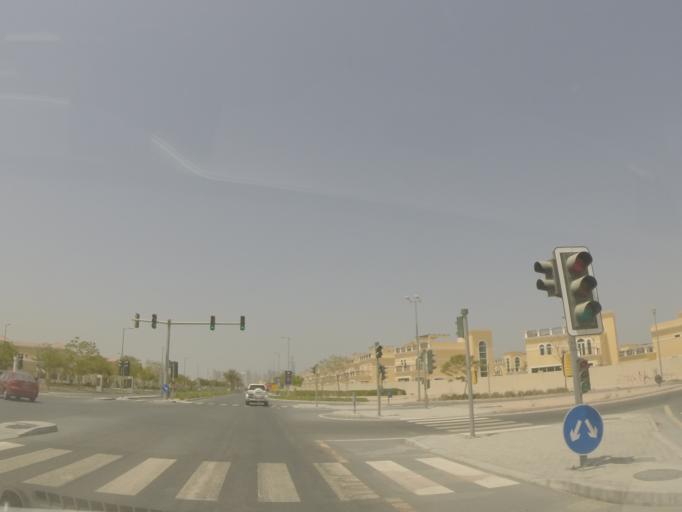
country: AE
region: Dubai
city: Dubai
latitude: 25.0419
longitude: 55.1696
